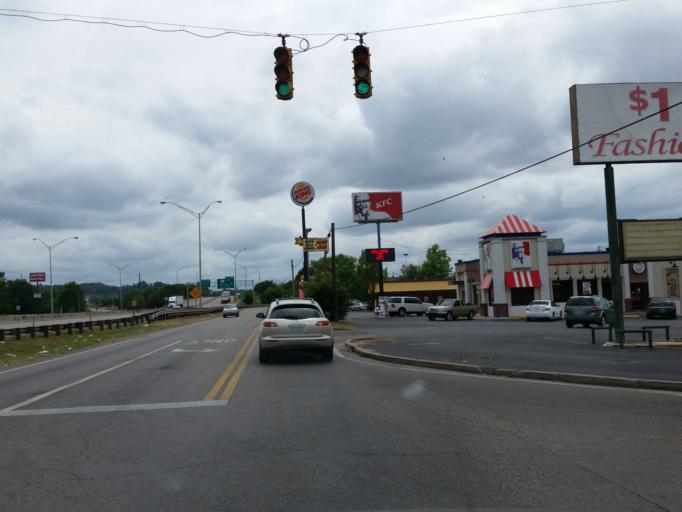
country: US
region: Mississippi
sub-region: Lauderdale County
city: Meridian
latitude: 32.3560
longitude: -88.6875
